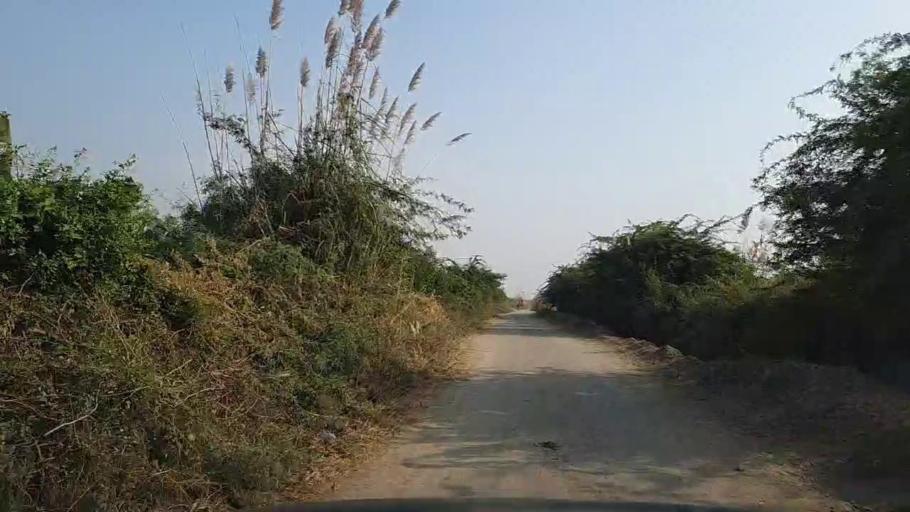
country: PK
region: Sindh
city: Thatta
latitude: 24.6508
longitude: 67.9238
